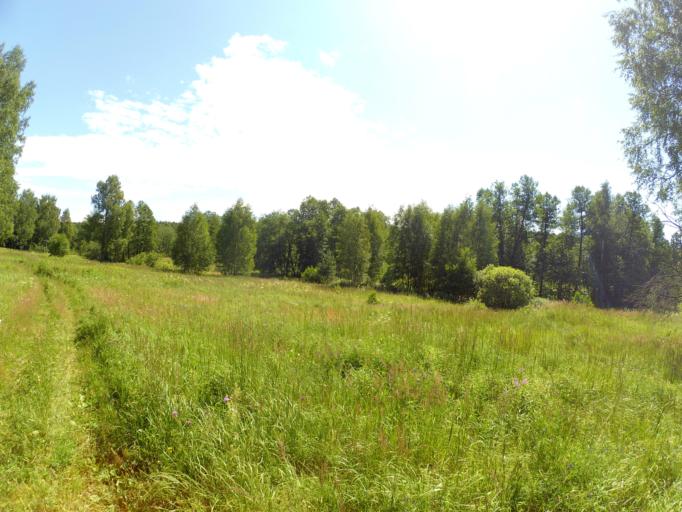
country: RU
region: Moskovskaya
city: Fosforitnyy
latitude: 55.3372
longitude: 38.9294
